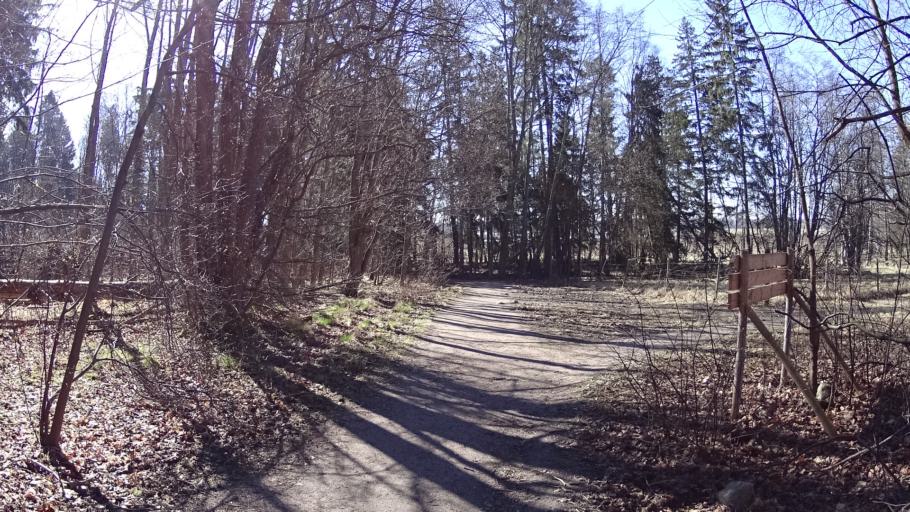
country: FI
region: Uusimaa
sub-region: Helsinki
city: Teekkarikylae
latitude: 60.2009
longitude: 24.8220
